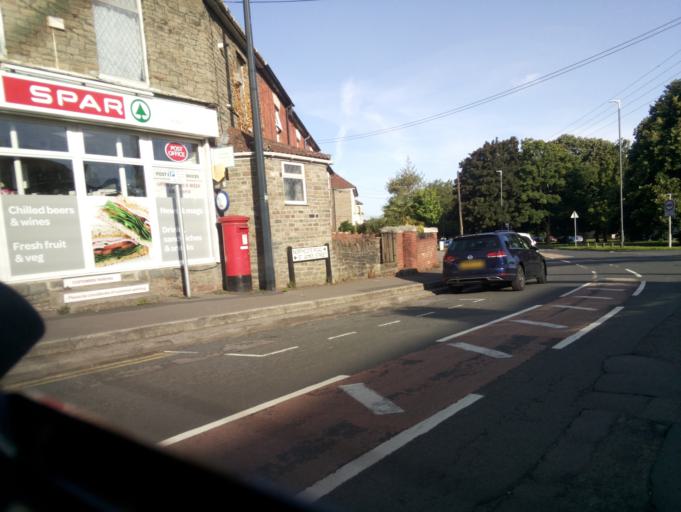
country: GB
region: England
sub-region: South Gloucestershire
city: Mangotsfield
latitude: 51.4855
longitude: -2.4871
